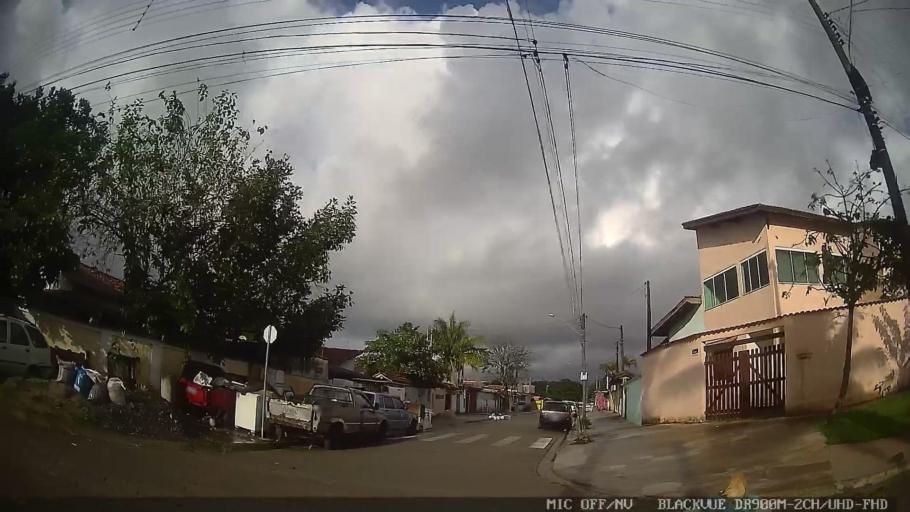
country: BR
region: Sao Paulo
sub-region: Itanhaem
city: Itanhaem
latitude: -24.2084
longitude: -46.8768
